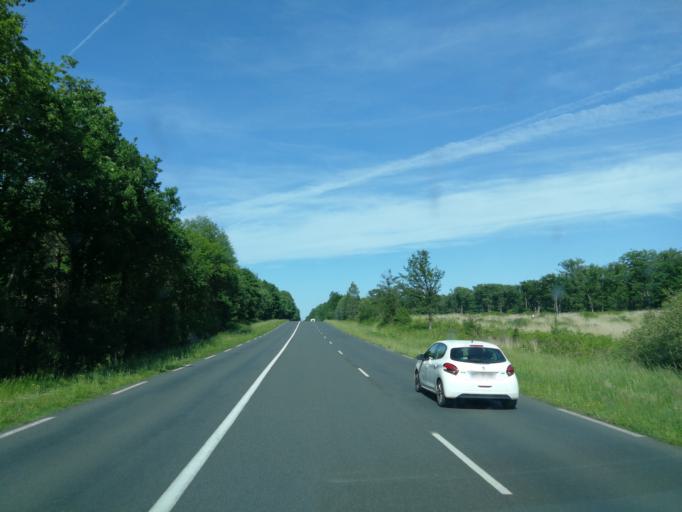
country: FR
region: Centre
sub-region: Departement d'Indre-et-Loire
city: Cheille
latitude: 47.2112
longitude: 0.3489
